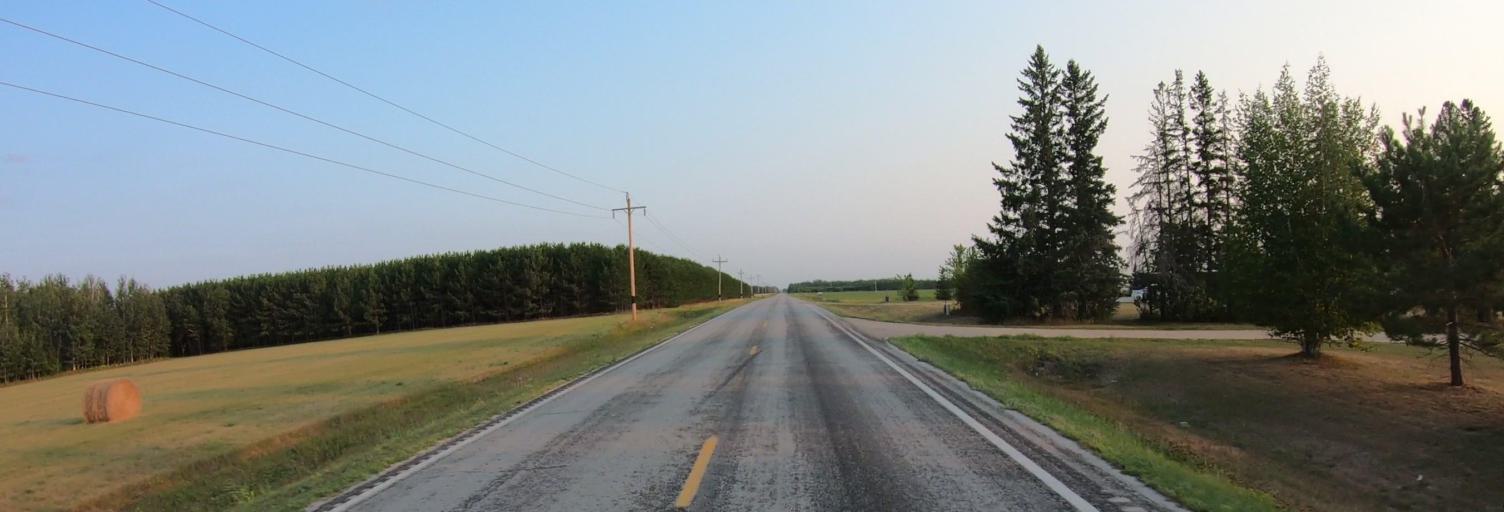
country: US
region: Minnesota
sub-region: Roseau County
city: Warroad
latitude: 48.8192
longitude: -95.3306
